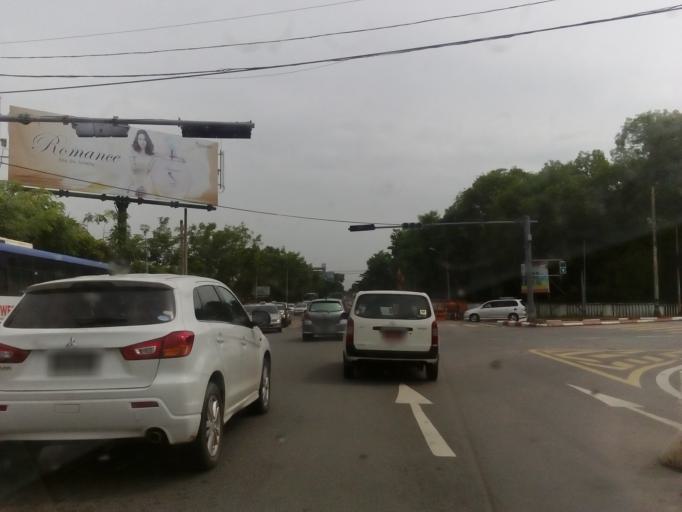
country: MM
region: Yangon
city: Yangon
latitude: 16.8328
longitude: 96.1551
